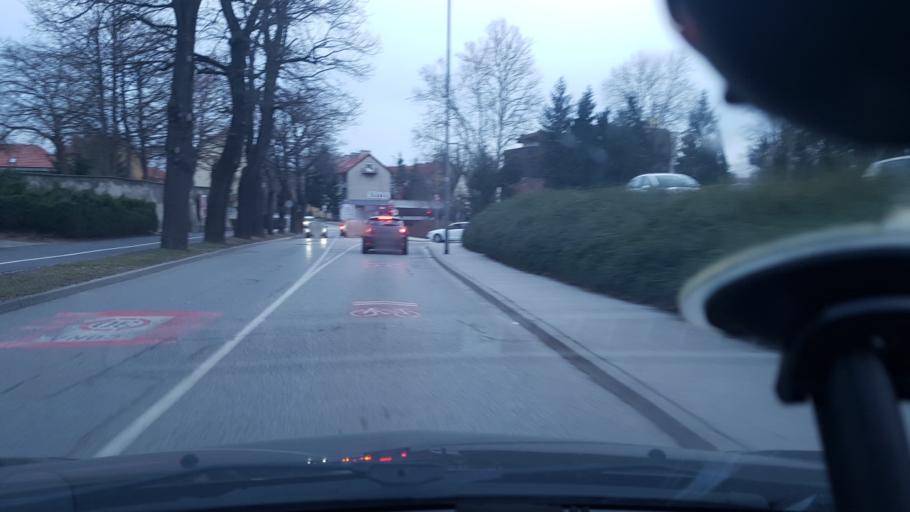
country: SI
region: Ptuj
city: Ptuj
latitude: 46.4238
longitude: 15.8740
